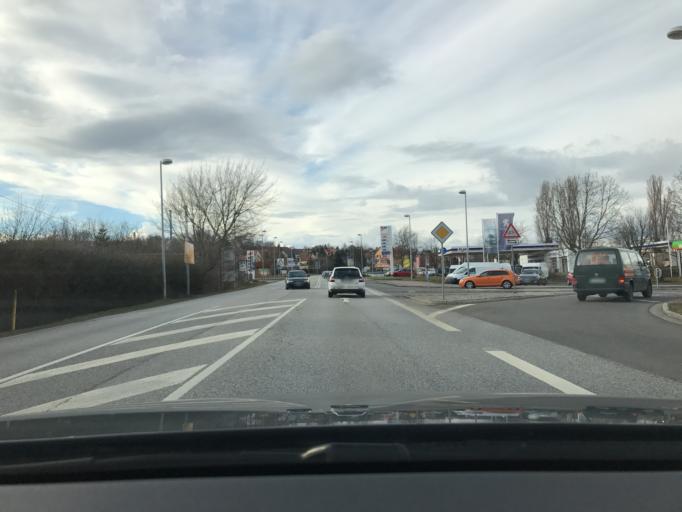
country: DE
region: Saxony-Anhalt
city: Volkstedt
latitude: 51.5115
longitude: 11.5720
